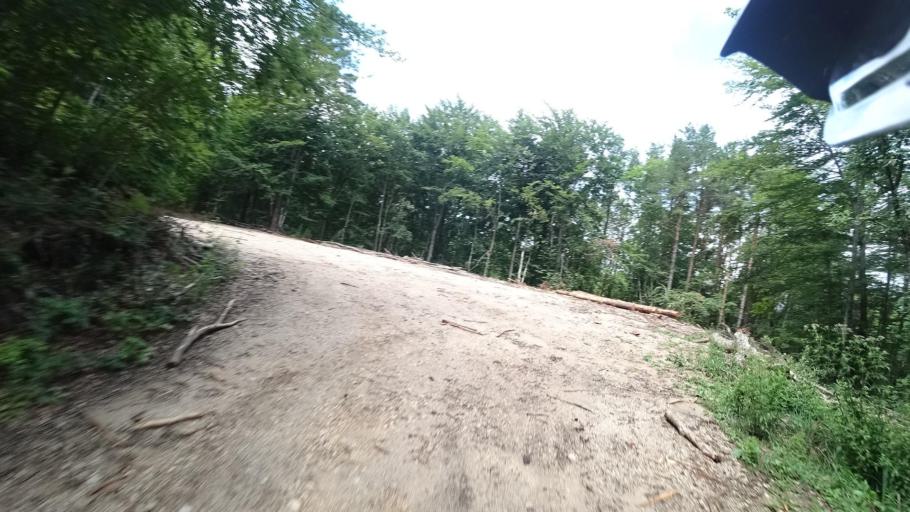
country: HR
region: Licko-Senjska
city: Otocac
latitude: 44.8741
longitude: 15.4101
